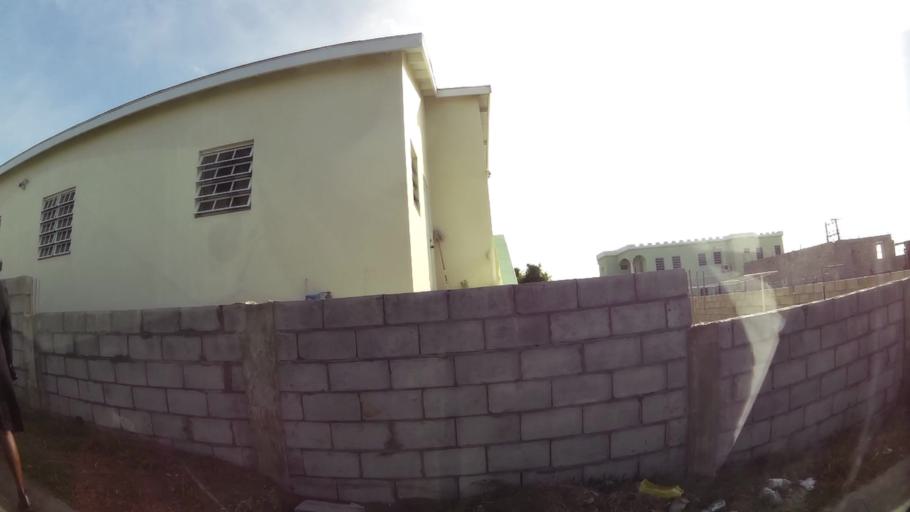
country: KN
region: Saint George Basseterre
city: Basseterre
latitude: 17.2929
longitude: -62.7395
